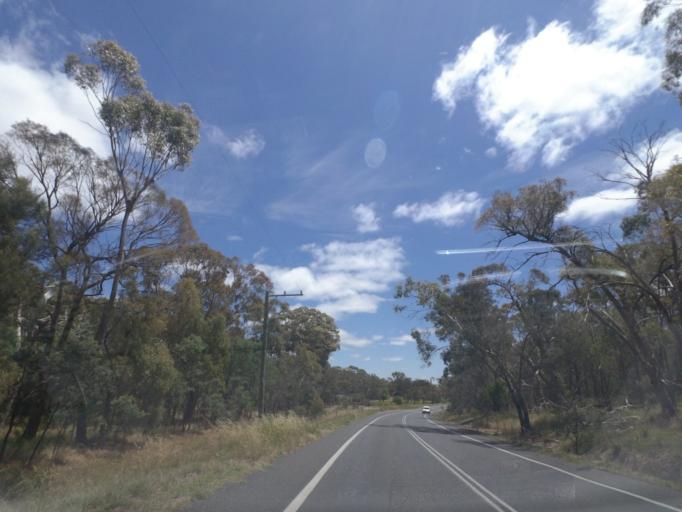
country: AU
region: Victoria
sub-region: Mount Alexander
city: Castlemaine
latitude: -37.2822
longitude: 144.1536
